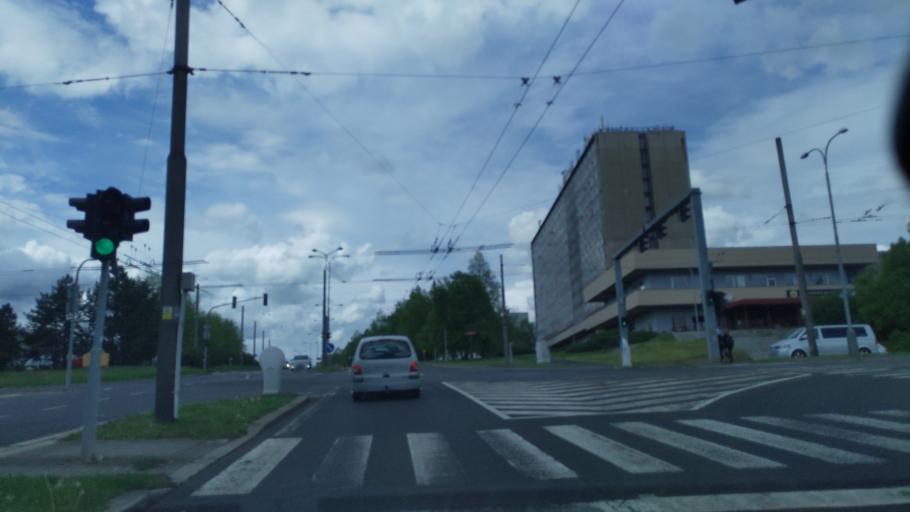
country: CZ
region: Ustecky
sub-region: Okres Usti nad Labem
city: Usti nad Labem
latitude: 50.6756
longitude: 14.0311
